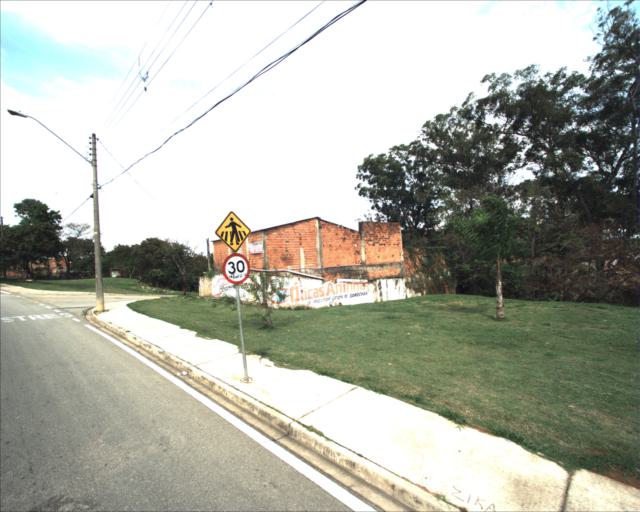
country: BR
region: Sao Paulo
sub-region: Sorocaba
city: Sorocaba
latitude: -23.5039
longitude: -47.4989
